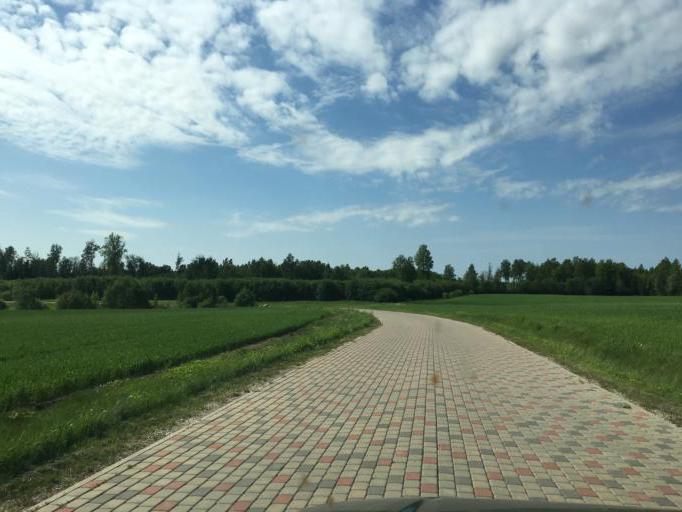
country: LV
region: Talsu Rajons
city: Valdemarpils
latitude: 57.3747
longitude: 22.5191
